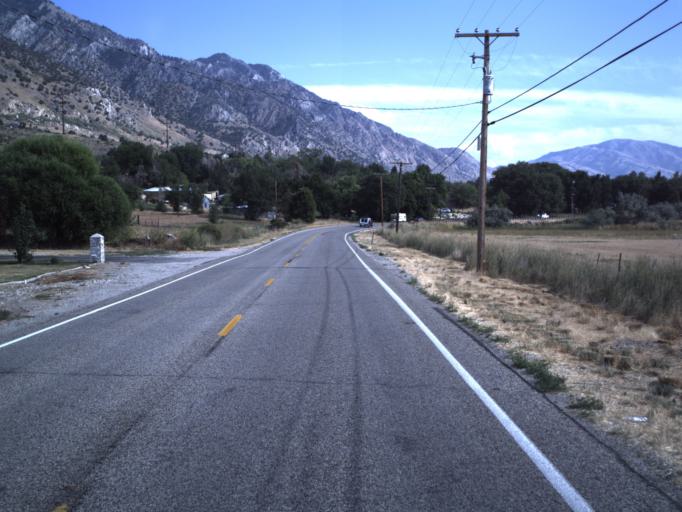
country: US
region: Utah
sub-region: Box Elder County
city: Honeyville
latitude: 41.5979
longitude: -112.0473
